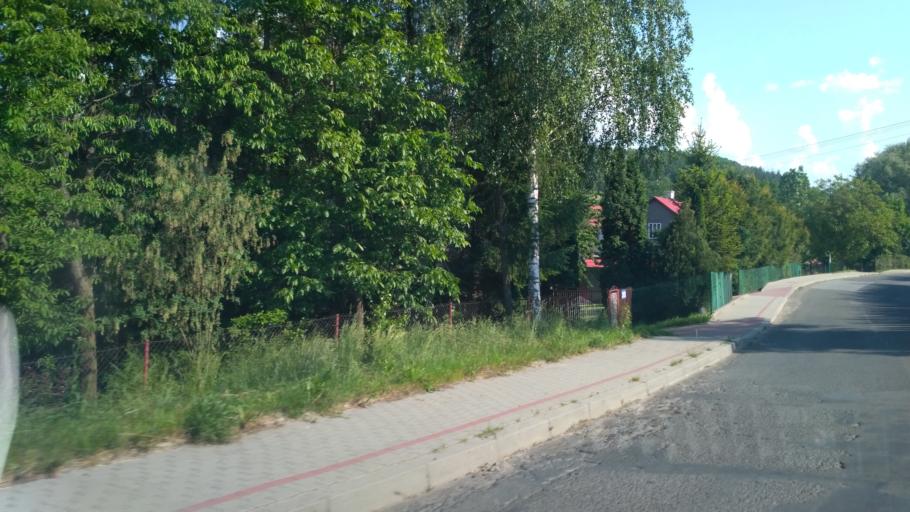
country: PL
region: Subcarpathian Voivodeship
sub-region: Powiat jaroslawski
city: Pruchnik
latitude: 49.8916
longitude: 22.4985
